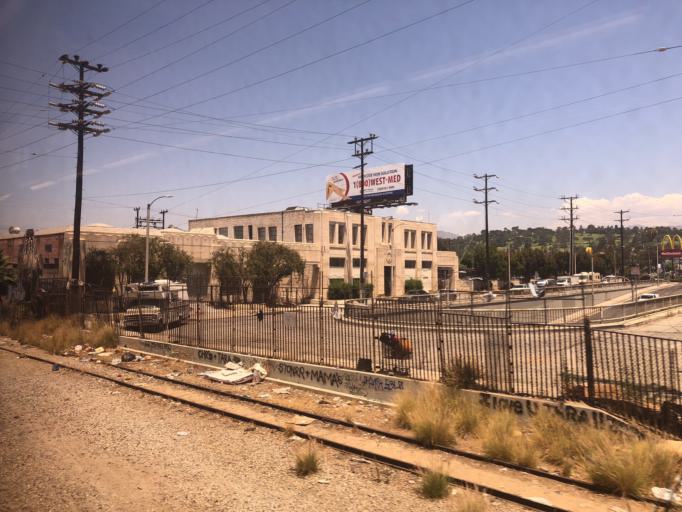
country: US
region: California
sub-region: Los Angeles County
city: Glendale
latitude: 34.1131
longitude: -118.2476
